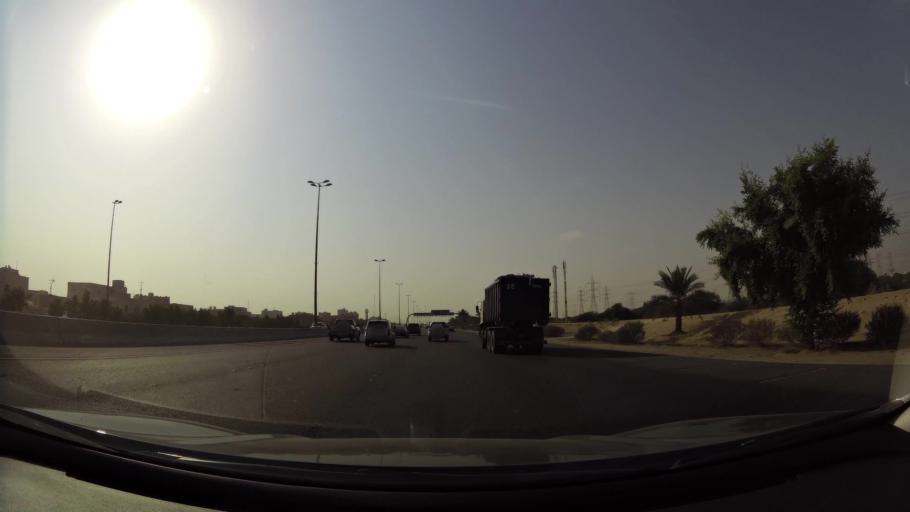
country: KW
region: Al Ahmadi
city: Al Ahmadi
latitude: 29.1033
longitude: 48.0962
